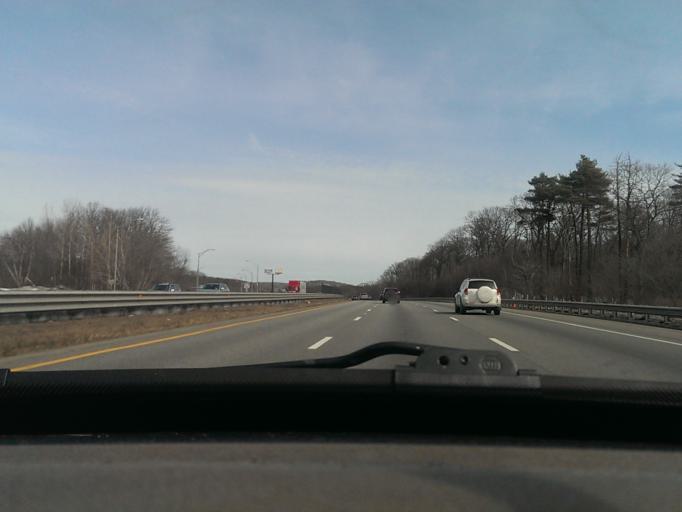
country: US
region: Massachusetts
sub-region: Worcester County
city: Charlton
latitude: 42.1545
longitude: -71.9668
